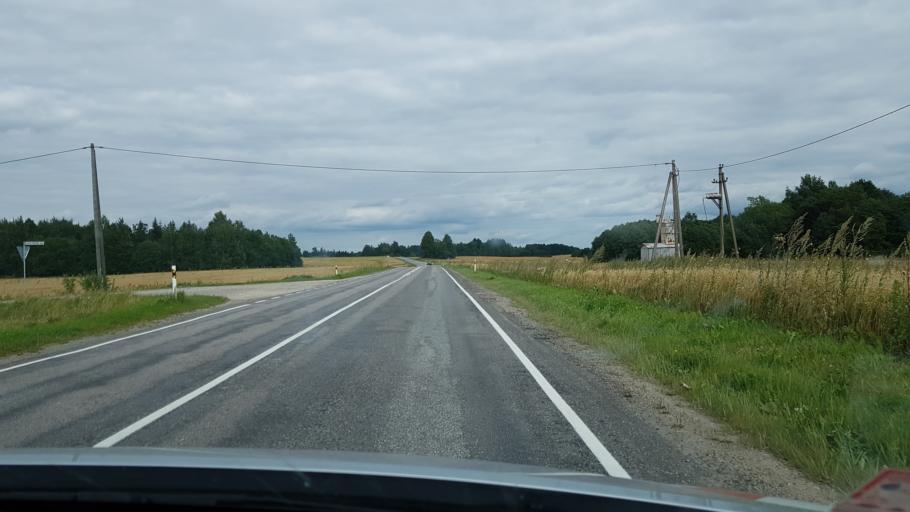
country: EE
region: Tartu
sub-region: Noo vald
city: Noo
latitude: 58.2148
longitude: 26.6064
